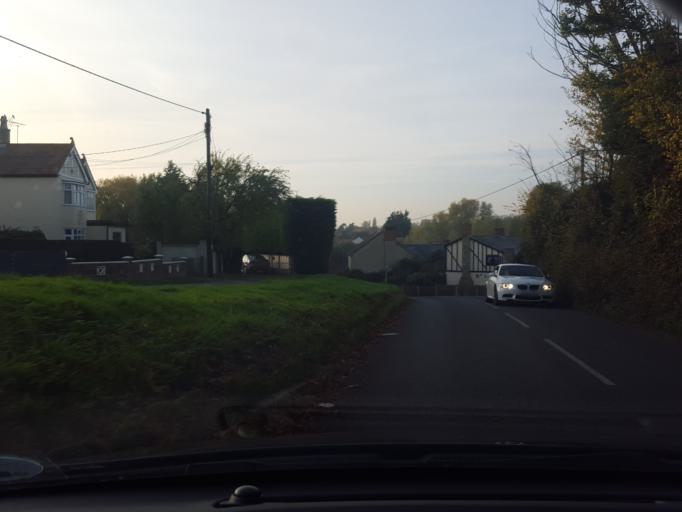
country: GB
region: England
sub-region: Essex
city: Saint Osyth
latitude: 51.7955
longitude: 1.0845
